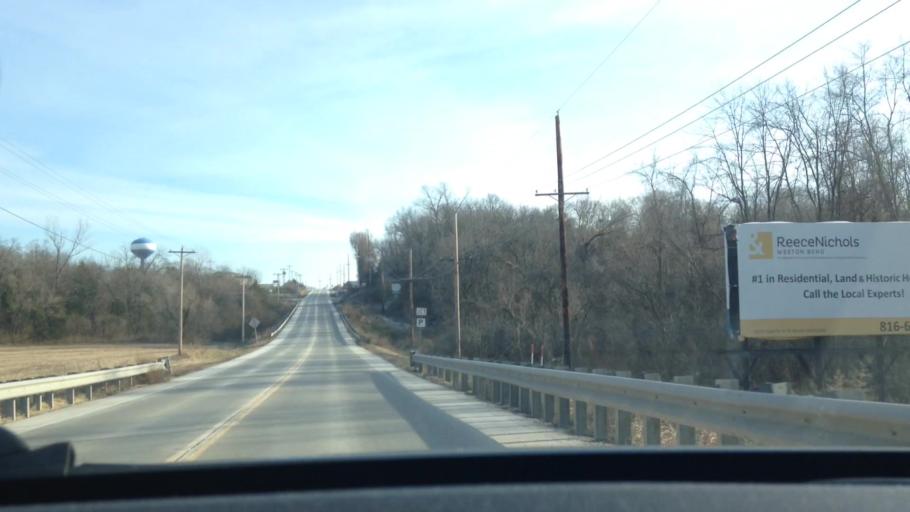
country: US
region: Missouri
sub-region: Platte County
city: Weston
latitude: 39.4199
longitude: -94.8939
